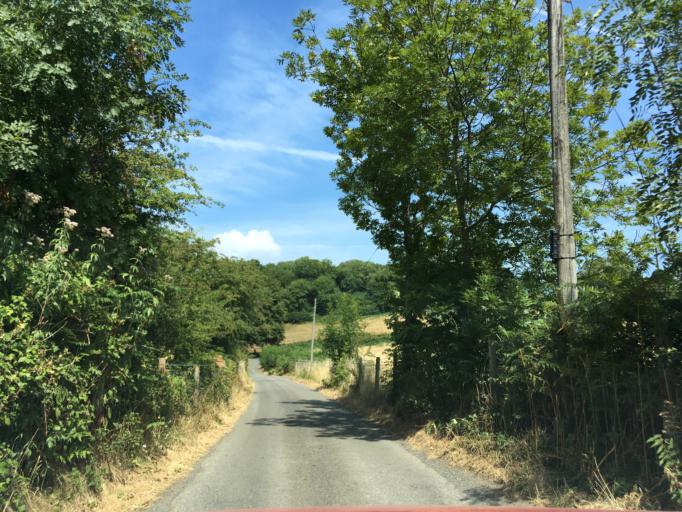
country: GB
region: Wales
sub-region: Caerphilly County Borough
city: Risca
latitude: 51.5883
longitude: -3.1120
